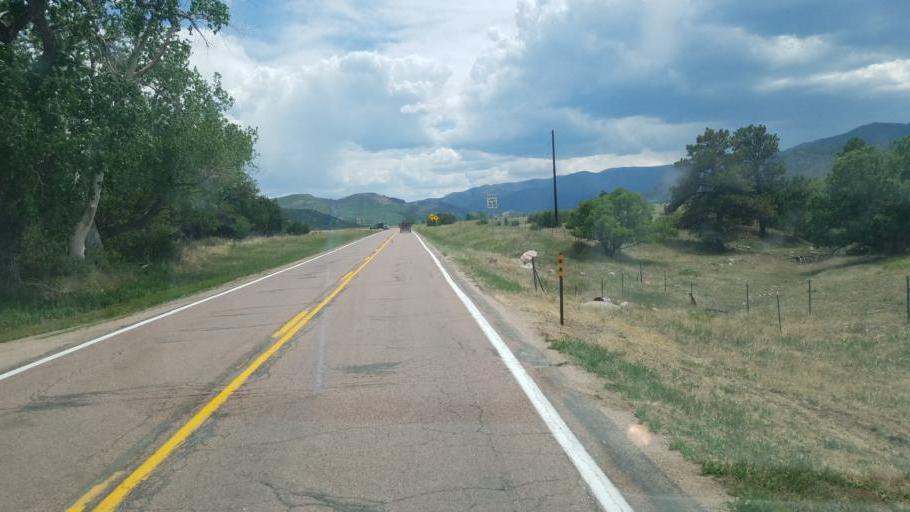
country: US
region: Colorado
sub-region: Fremont County
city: Florence
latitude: 38.2471
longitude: -105.0904
